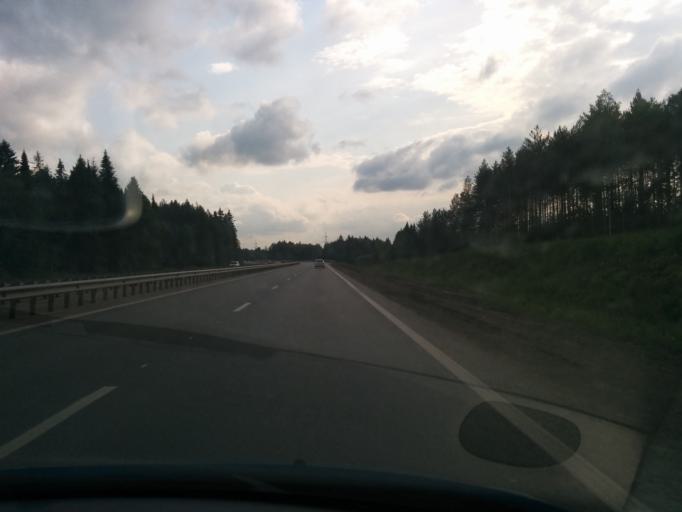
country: RU
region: Perm
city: Ferma
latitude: 58.0154
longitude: 56.4090
